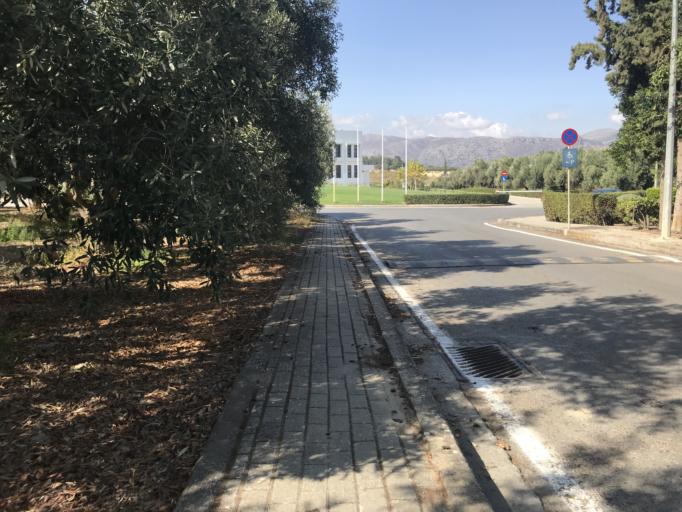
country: GR
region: Crete
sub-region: Nomos Irakleiou
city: Gazi
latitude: 35.3054
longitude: 25.0737
